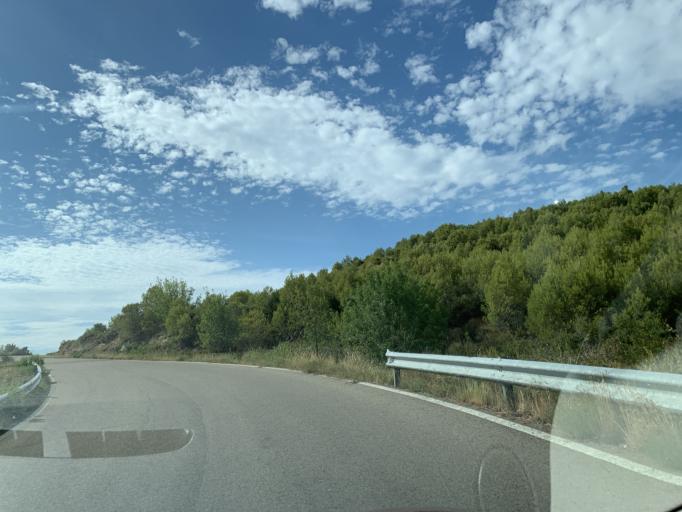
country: ES
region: Aragon
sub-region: Provincia de Zaragoza
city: Santa Eulalia de Gallego
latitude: 42.3271
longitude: -0.7215
